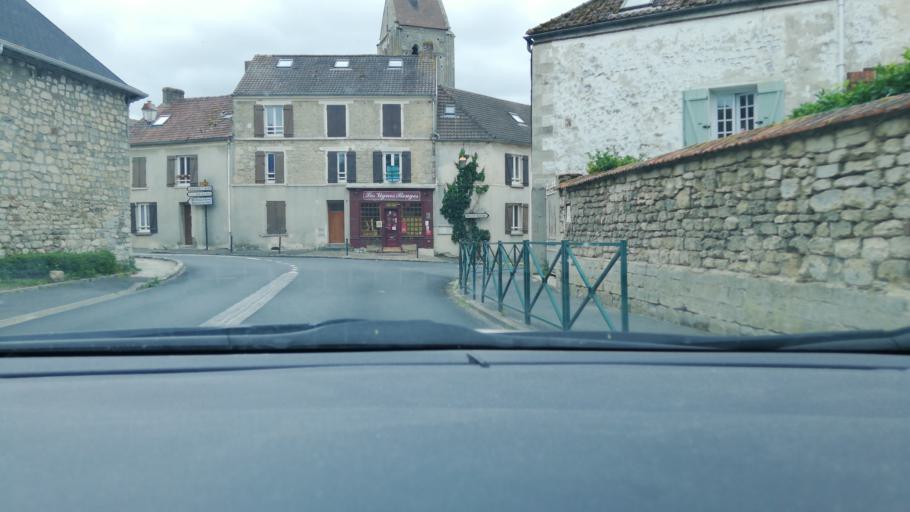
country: FR
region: Ile-de-France
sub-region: Departement du Val-d'Oise
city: Ennery
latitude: 49.1014
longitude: 2.1321
